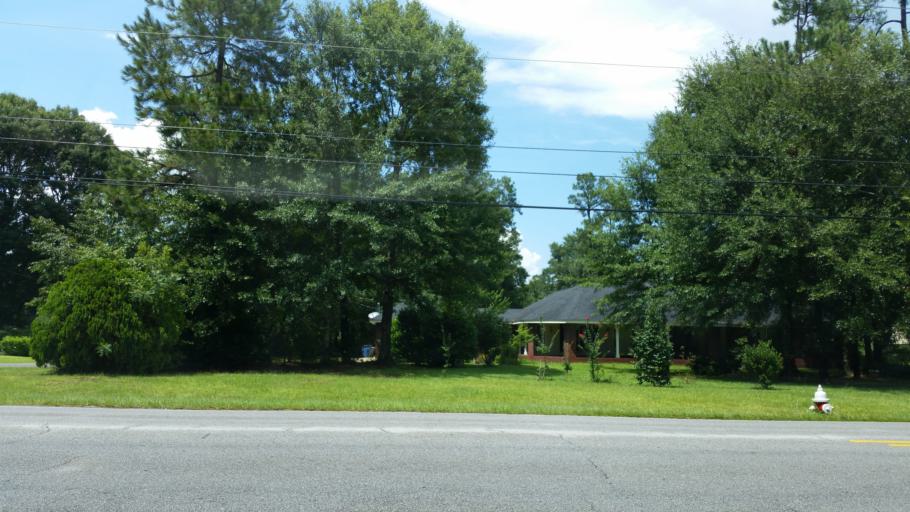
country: US
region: Florida
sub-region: Escambia County
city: Gonzalez
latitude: 30.5629
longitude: -87.2976
